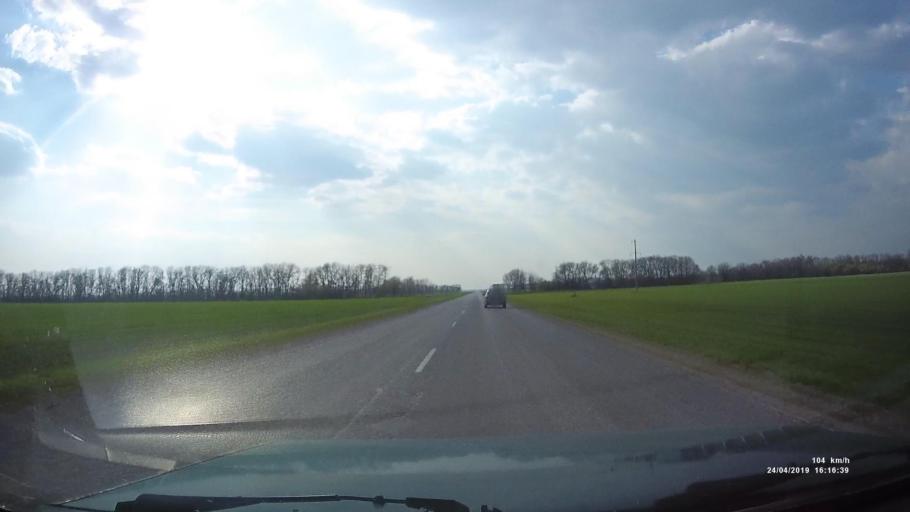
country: RU
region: Rostov
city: Sovetskoye
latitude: 46.7654
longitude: 42.1541
